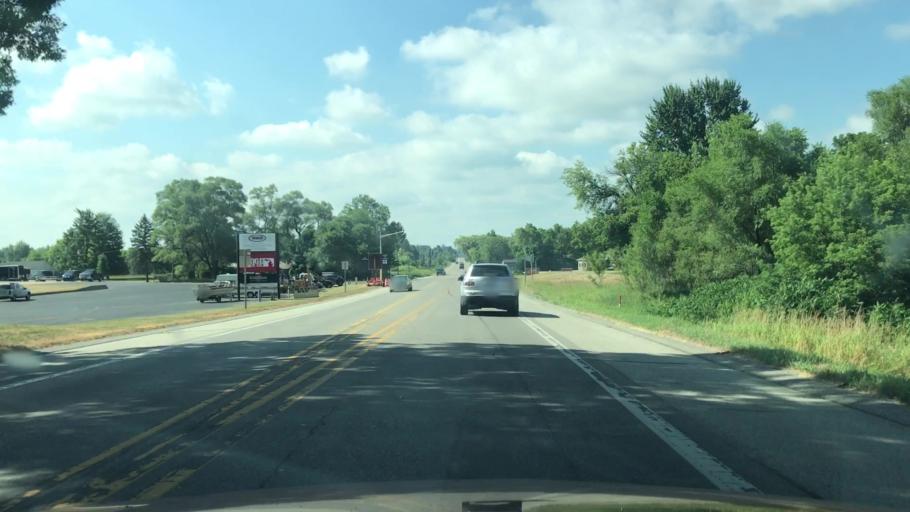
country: US
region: Michigan
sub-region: Kent County
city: Kent City
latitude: 43.3089
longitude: -85.8106
